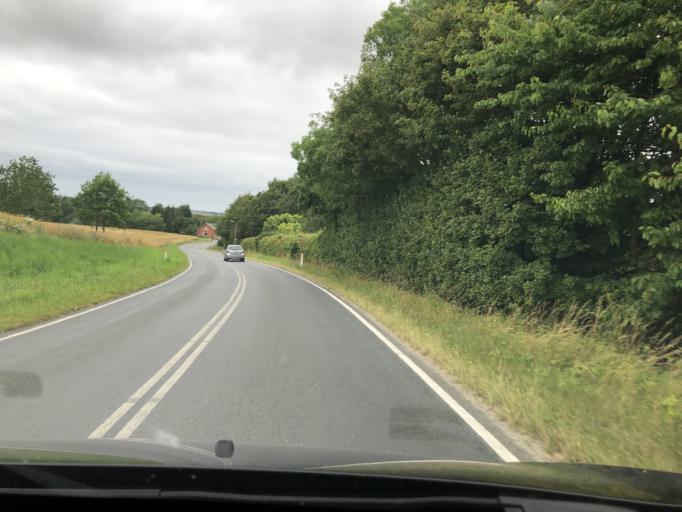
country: DK
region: South Denmark
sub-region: AEro Kommune
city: AEroskobing
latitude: 54.9107
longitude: 10.2891
